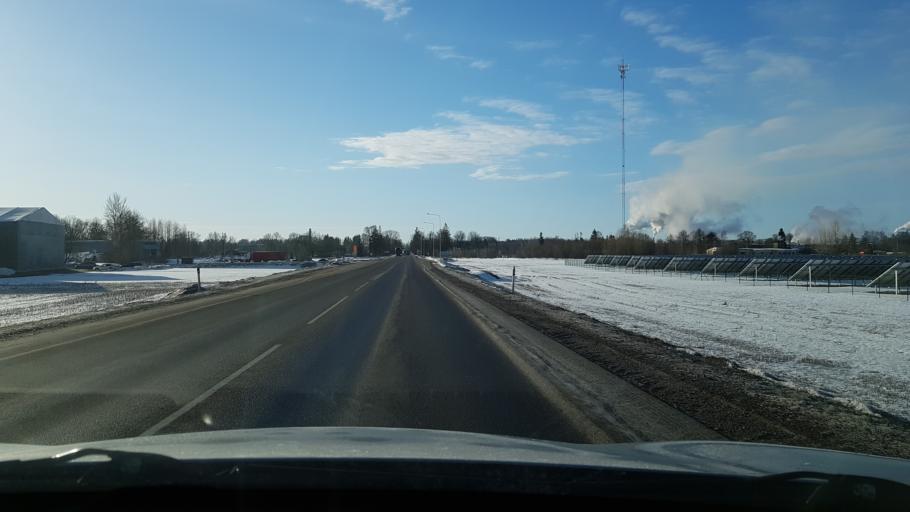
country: EE
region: Jogevamaa
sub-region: Poltsamaa linn
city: Poltsamaa
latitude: 58.7408
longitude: 25.7685
